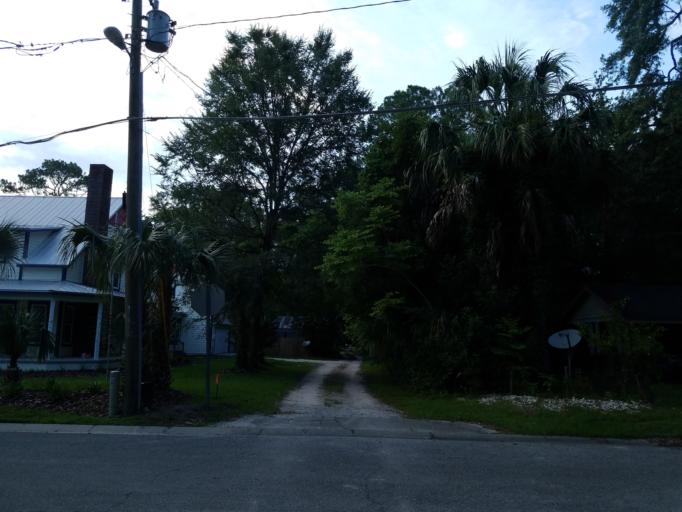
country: US
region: Florida
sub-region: Alachua County
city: Gainesville
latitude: 29.5048
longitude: -82.2831
